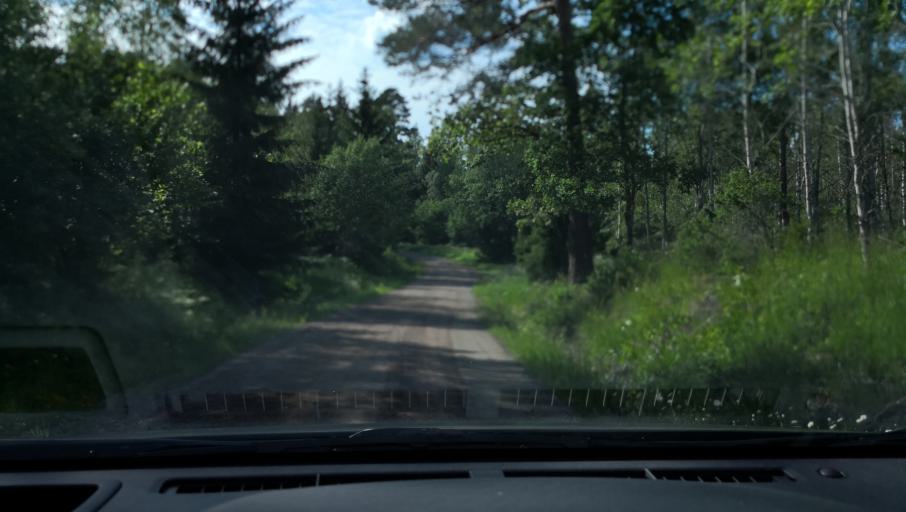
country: SE
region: Uppsala
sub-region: Enkopings Kommun
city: Orsundsbro
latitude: 59.8349
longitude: 17.2328
